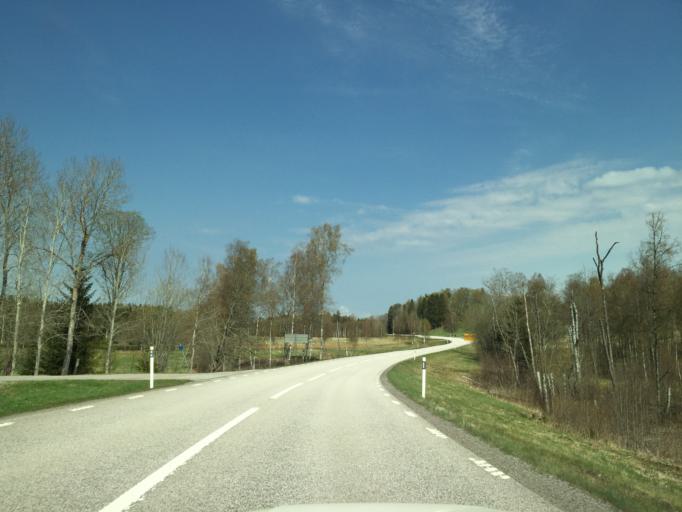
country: SE
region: Vaestra Goetaland
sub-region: Bengtsfors Kommun
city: Dals Langed
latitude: 58.8610
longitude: 12.1853
